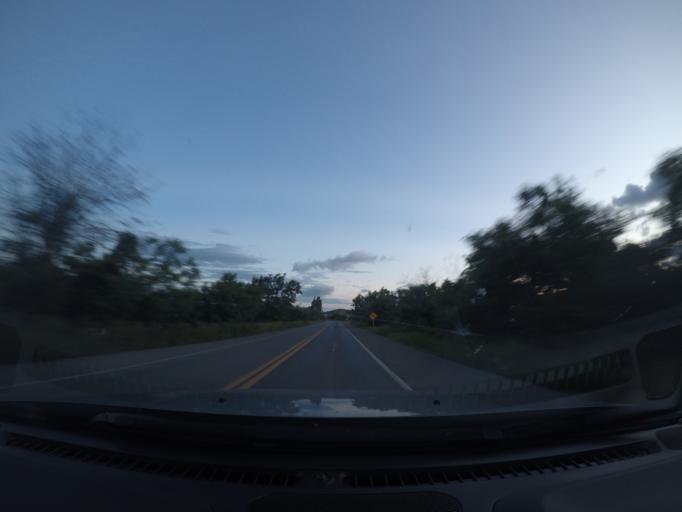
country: BR
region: Bahia
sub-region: Seabra
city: Seabra
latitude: -12.4558
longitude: -41.7498
